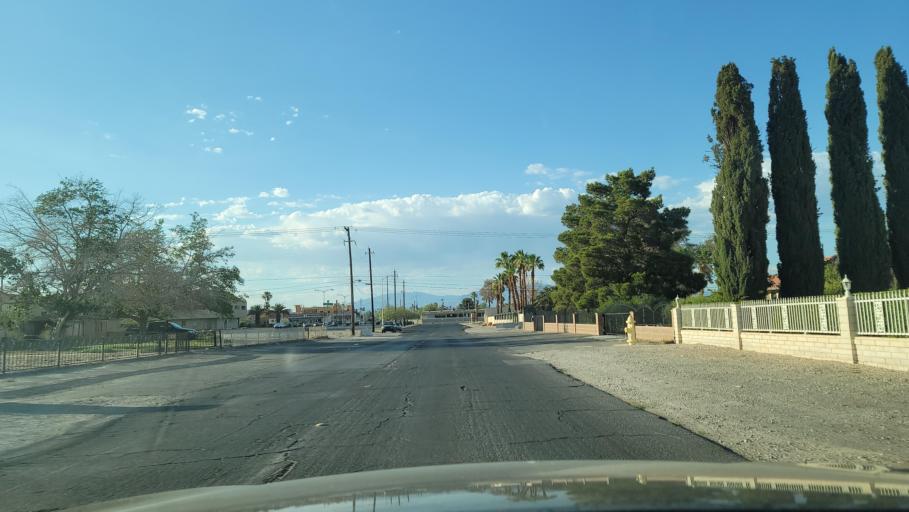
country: US
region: Nevada
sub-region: Clark County
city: Spring Valley
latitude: 36.1568
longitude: -115.2191
